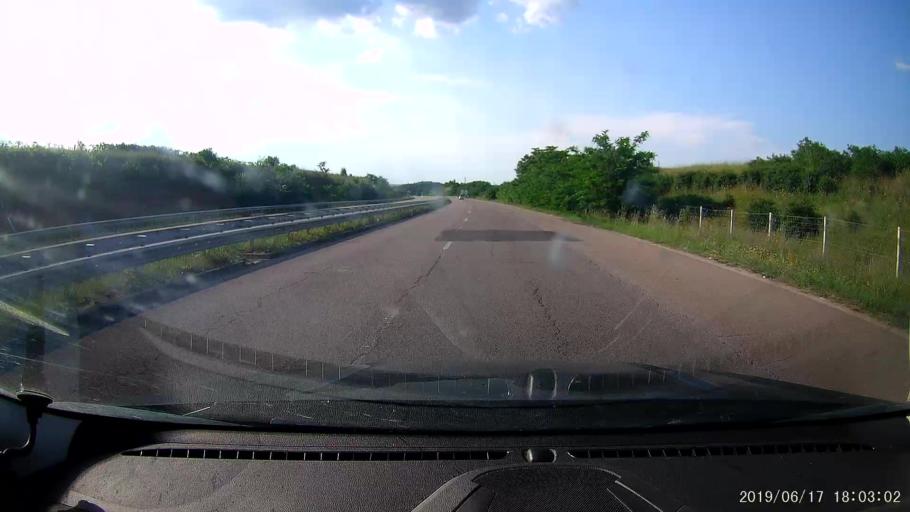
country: BG
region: Khaskovo
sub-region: Obshtina Svilengrad
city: Svilengrad
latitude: 41.7712
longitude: 26.2249
